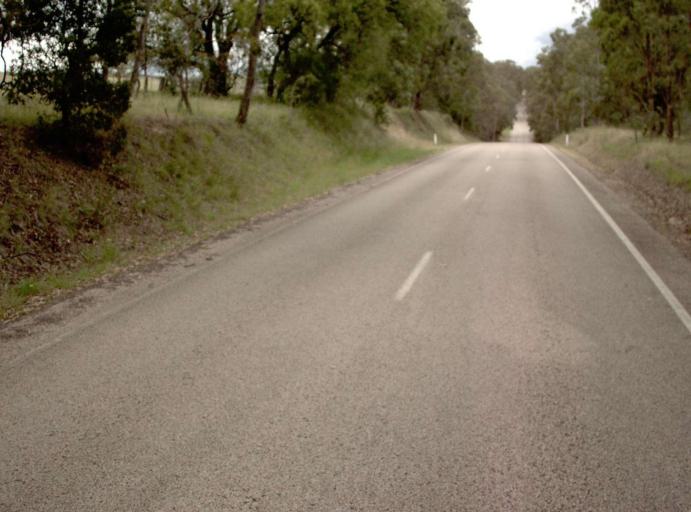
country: AU
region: Victoria
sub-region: East Gippsland
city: Bairnsdale
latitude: -37.5513
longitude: 147.1987
